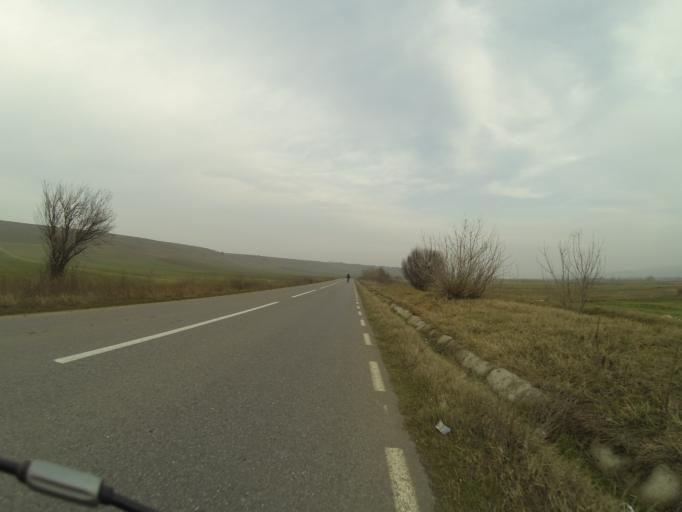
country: RO
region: Mehedinti
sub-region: Comuna Corlatel
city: Corlatel
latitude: 44.4094
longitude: 22.9540
